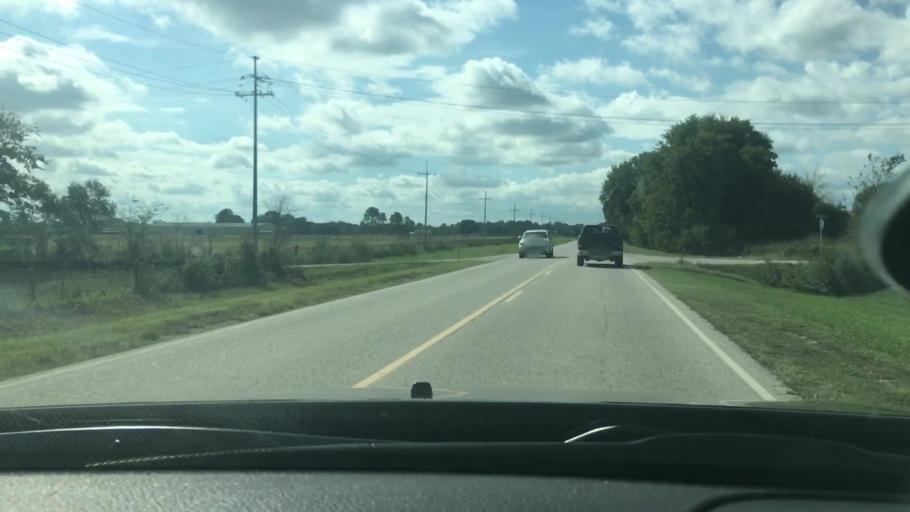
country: US
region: Oklahoma
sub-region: Pontotoc County
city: Ada
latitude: 34.6950
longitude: -96.6349
